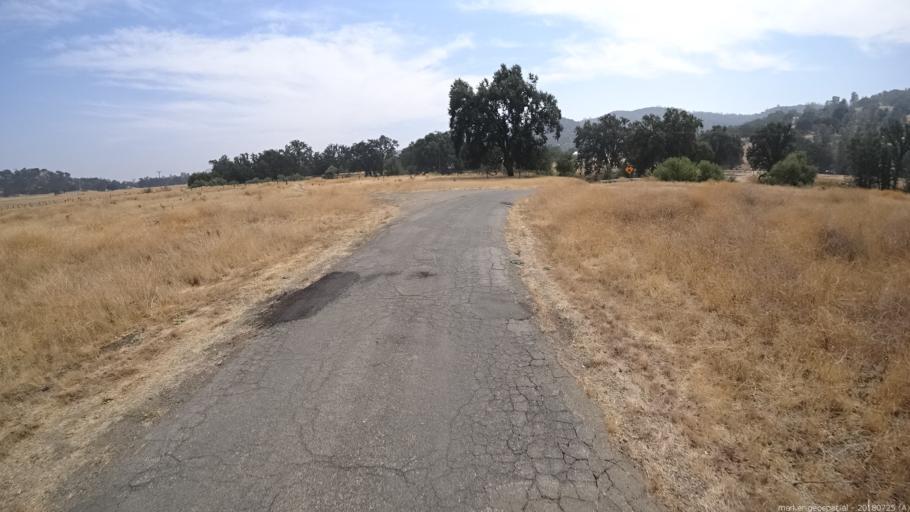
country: US
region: California
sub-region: Fresno County
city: Coalinga
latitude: 36.1954
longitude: -120.7076
